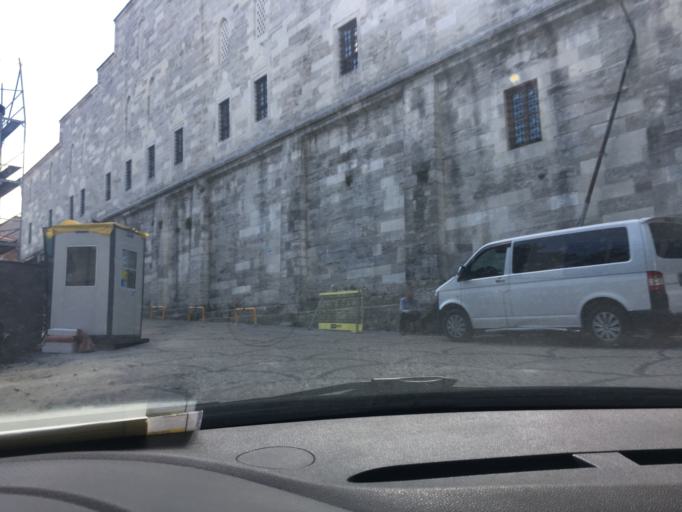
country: TR
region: Istanbul
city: Eminoenue
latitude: 41.0173
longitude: 28.9624
